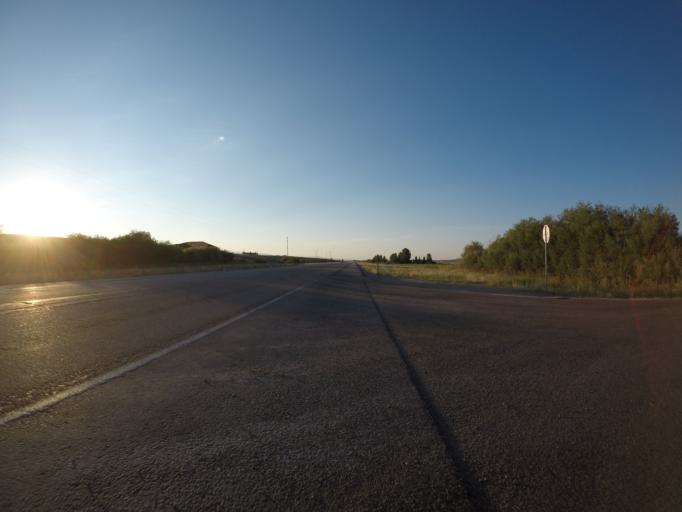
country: US
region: Wyoming
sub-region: Sublette County
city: Pinedale
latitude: 42.8085
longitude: -109.8257
